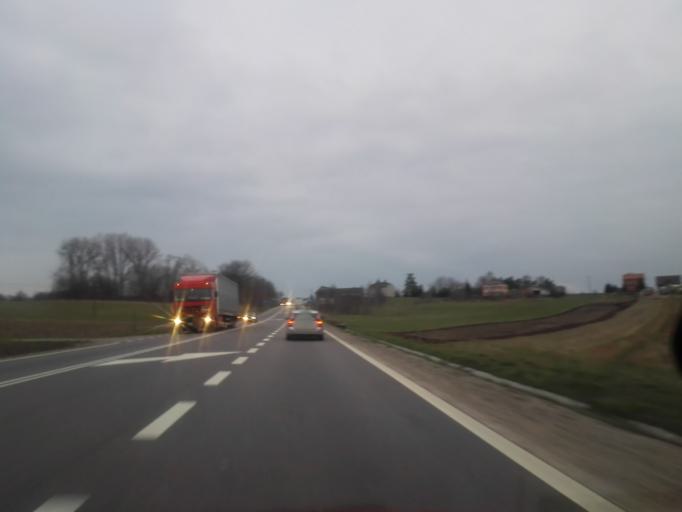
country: PL
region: Podlasie
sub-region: Powiat lomzynski
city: Piatnica
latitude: 53.2328
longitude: 22.1130
